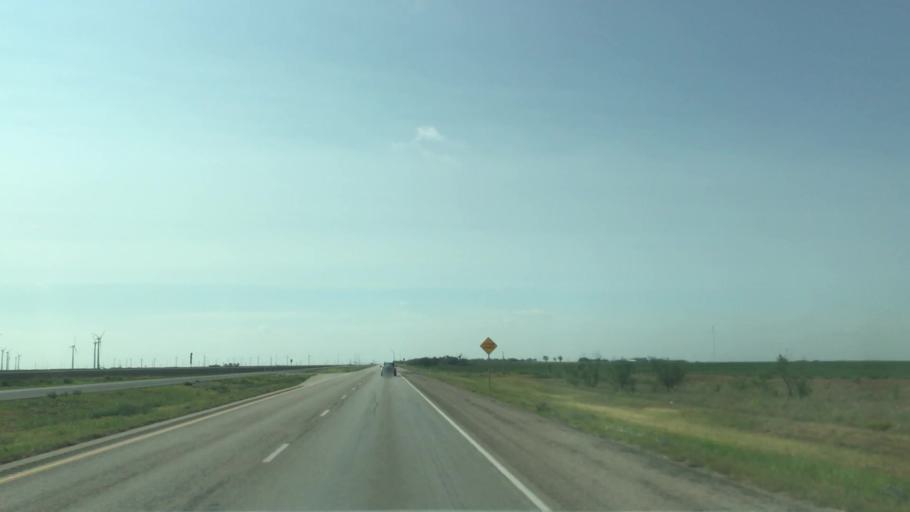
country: US
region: Texas
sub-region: Scurry County
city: Snyder
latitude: 32.6289
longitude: -100.7602
